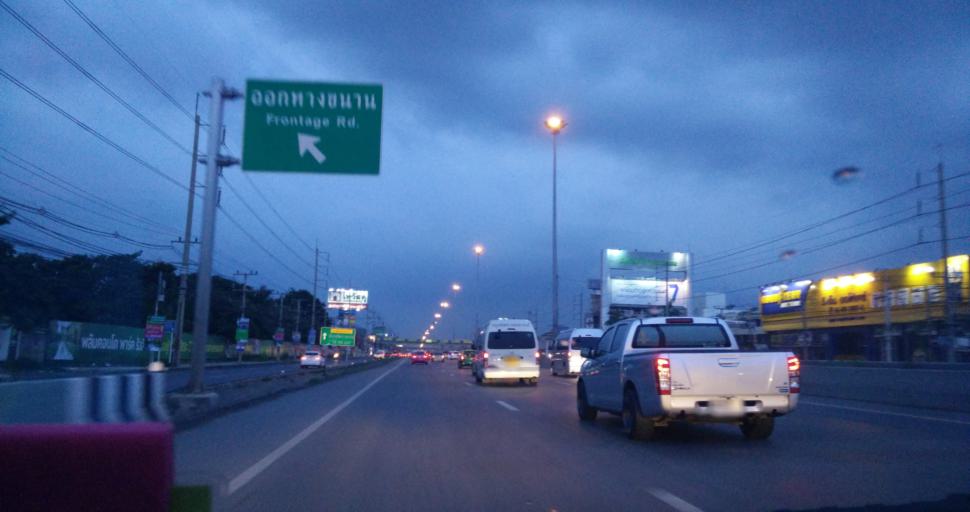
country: TH
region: Pathum Thani
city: Khlong Luang
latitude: 14.0123
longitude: 100.6152
